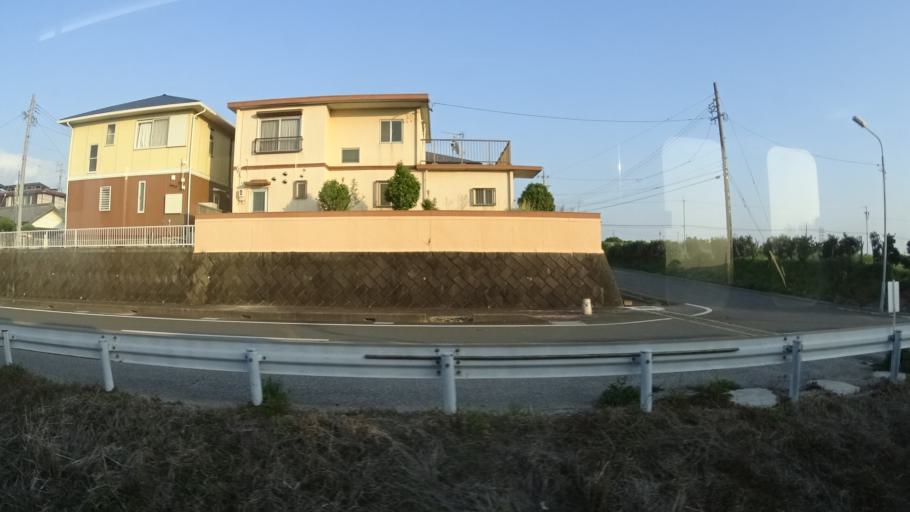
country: JP
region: Aichi
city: Tahara
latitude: 34.6723
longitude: 137.3052
